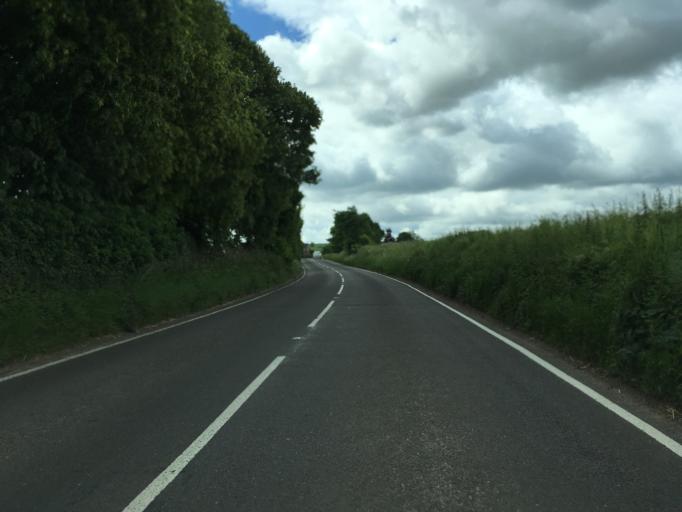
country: GB
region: England
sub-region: Oxfordshire
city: Shipton under Wychwood
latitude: 51.8519
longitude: -1.6014
